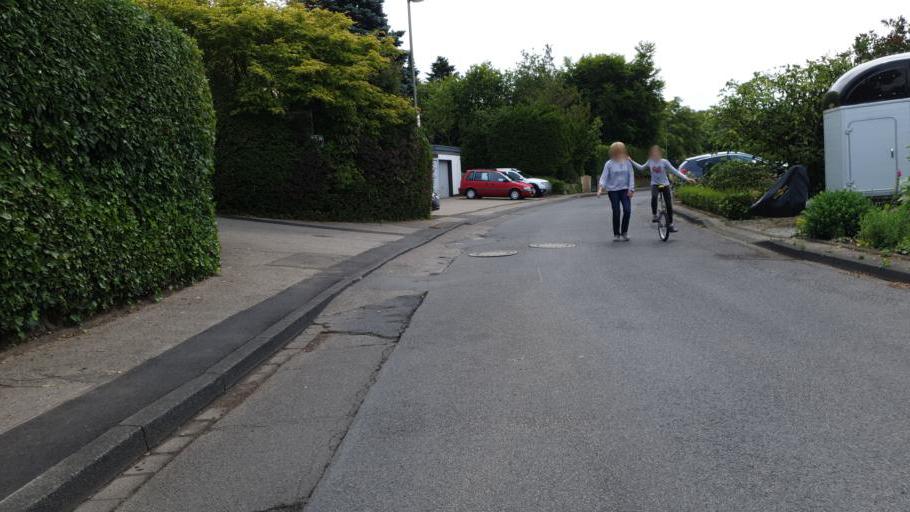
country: DE
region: North Rhine-Westphalia
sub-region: Regierungsbezirk Koln
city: Odenthal
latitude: 51.0171
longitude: 7.1083
